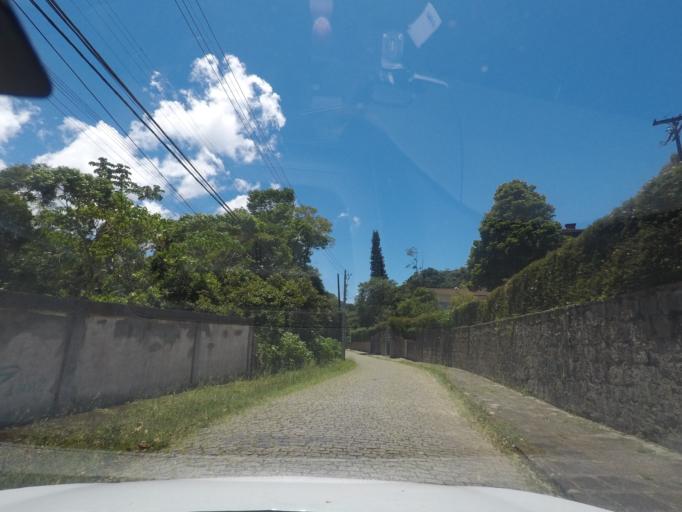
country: BR
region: Rio de Janeiro
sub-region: Teresopolis
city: Teresopolis
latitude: -22.4330
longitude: -42.9910
